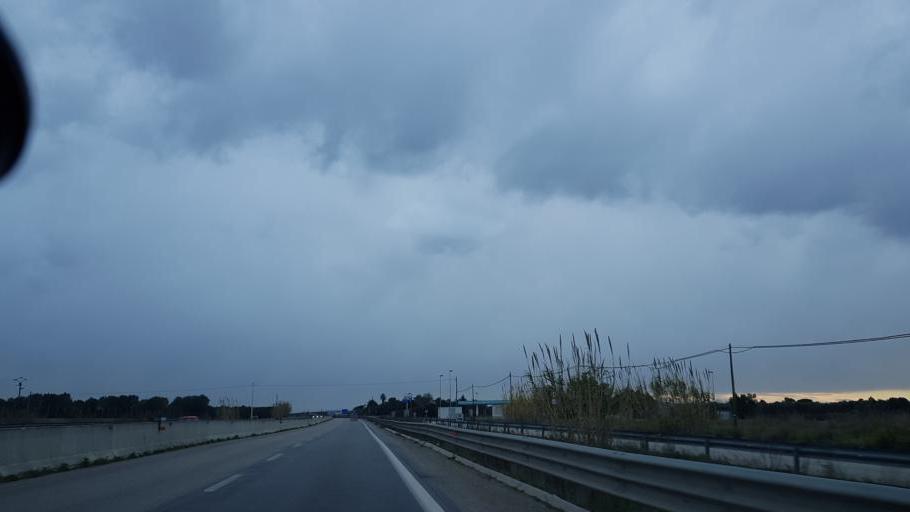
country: IT
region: Apulia
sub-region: Provincia di Brindisi
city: Brindisi
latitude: 40.5985
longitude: 17.8723
